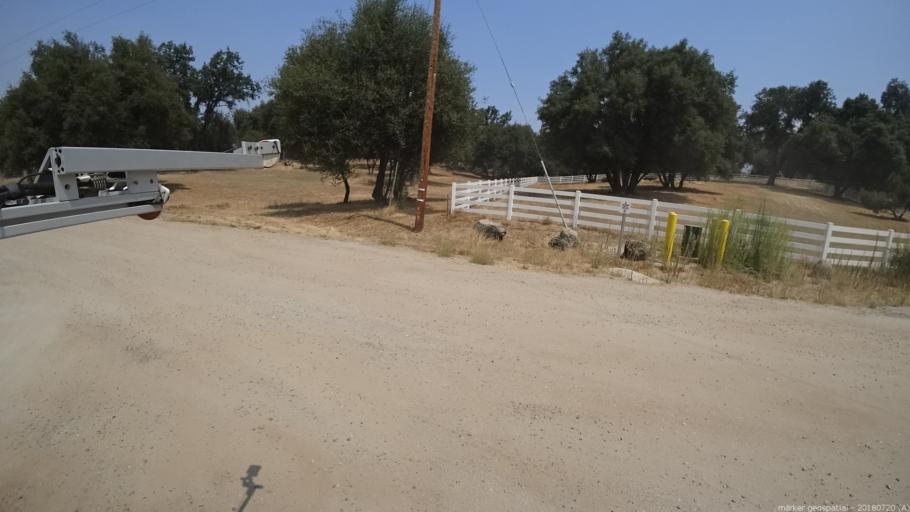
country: US
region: California
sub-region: Madera County
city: Ahwahnee
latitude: 37.3545
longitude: -119.7161
